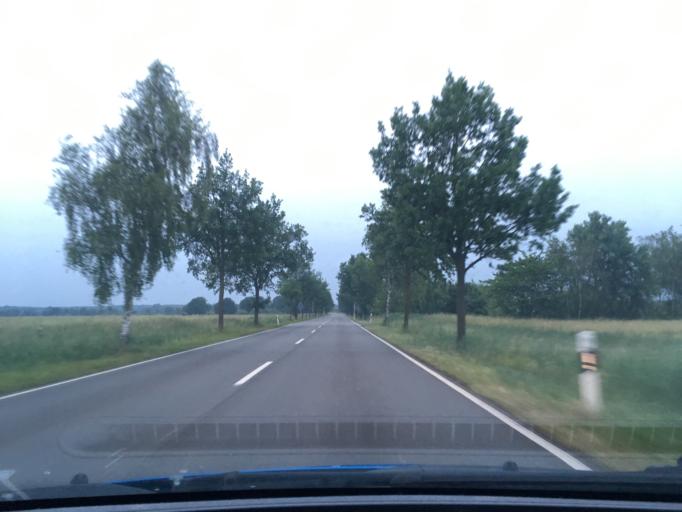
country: DE
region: Lower Saxony
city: Lubbow
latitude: 52.8948
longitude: 11.1788
